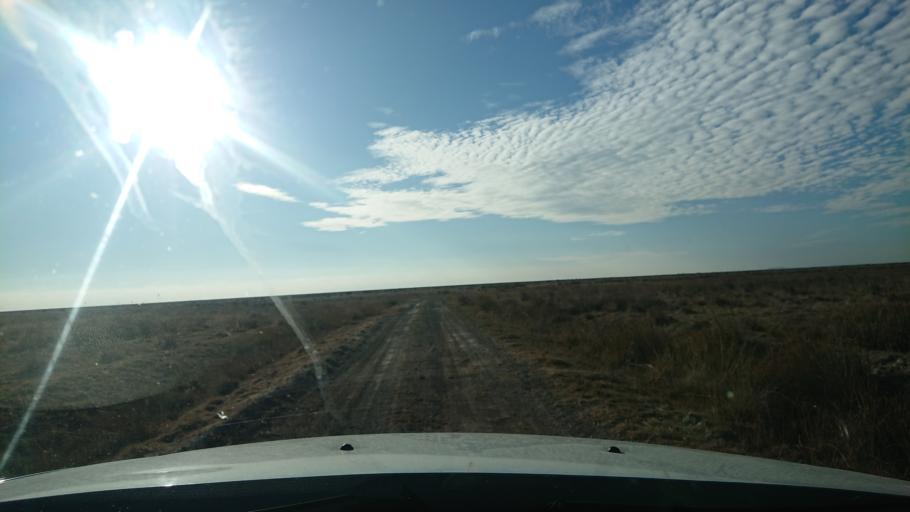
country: TR
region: Aksaray
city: Eskil
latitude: 38.5402
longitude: 33.3413
